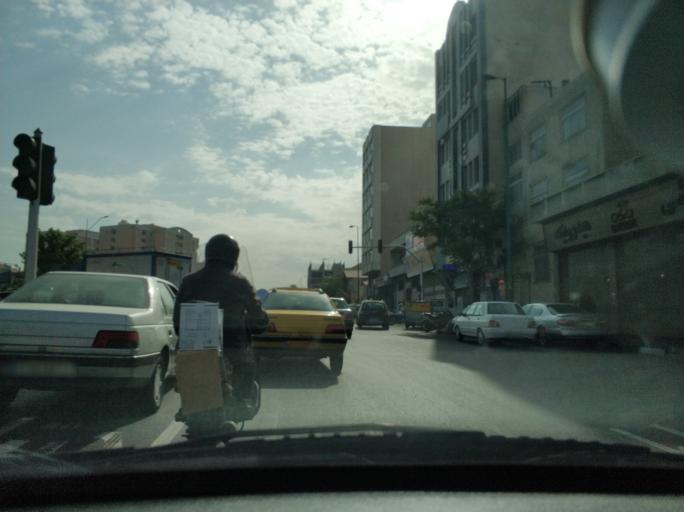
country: IR
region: Tehran
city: Tehran
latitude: 35.7208
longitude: 51.5108
